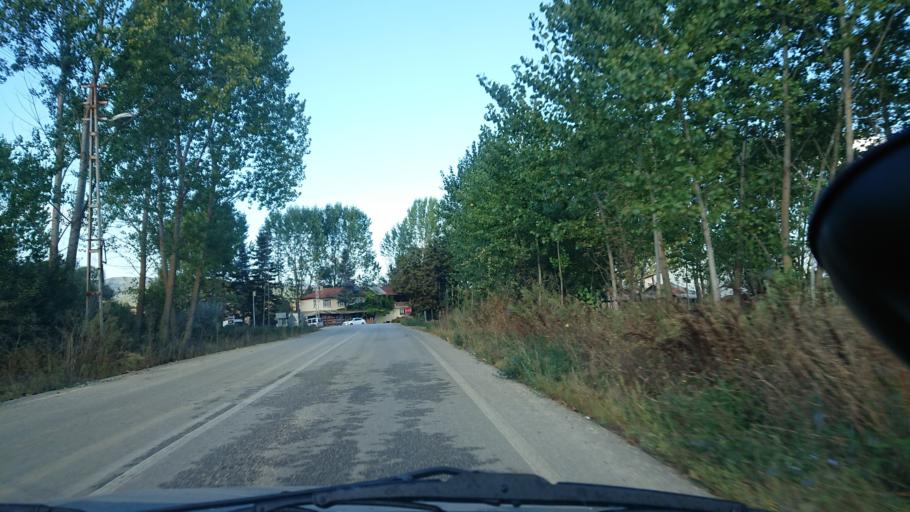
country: TR
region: Bilecik
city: Pazaryeri
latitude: 40.0159
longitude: 29.8356
